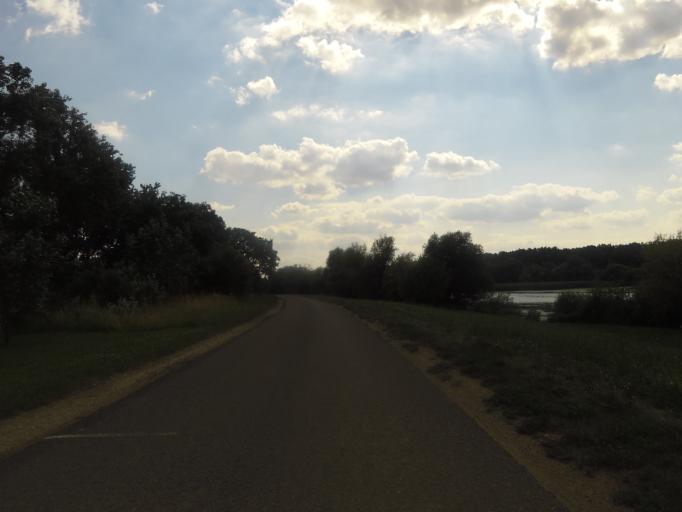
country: HU
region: Jasz-Nagykun-Szolnok
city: Tiszafured
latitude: 47.6197
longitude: 20.7278
